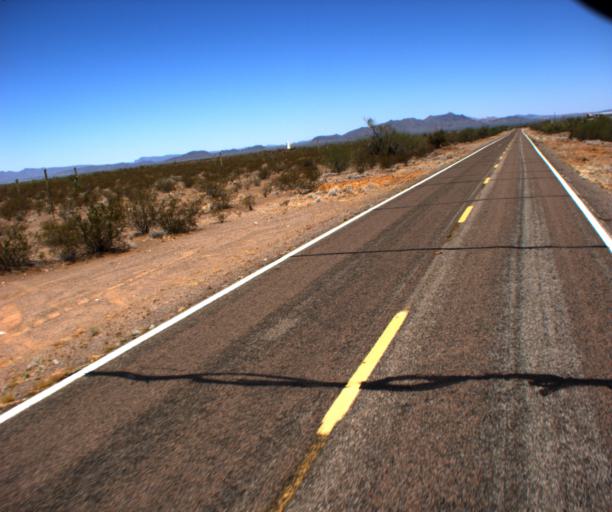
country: US
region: Arizona
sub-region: Pima County
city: Ajo
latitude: 32.2383
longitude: -112.7211
